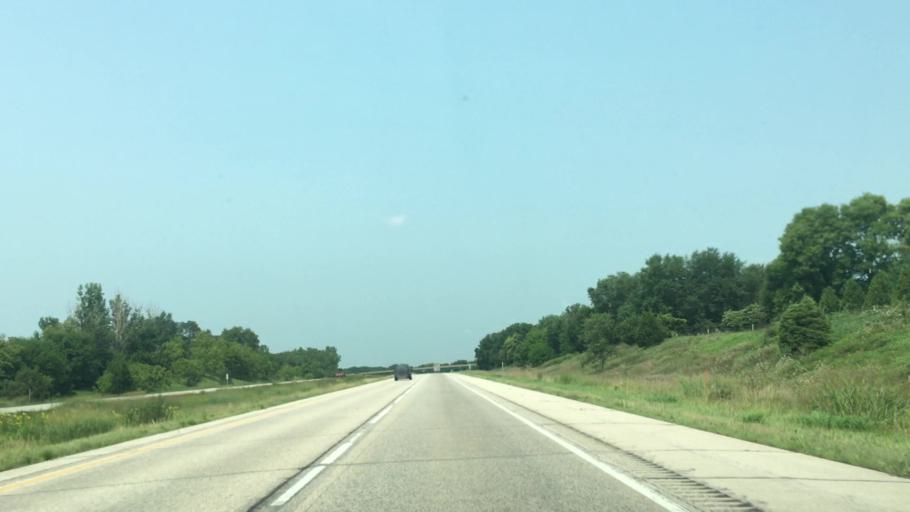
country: US
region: Iowa
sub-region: Linn County
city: Robins
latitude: 42.1201
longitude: -91.7137
